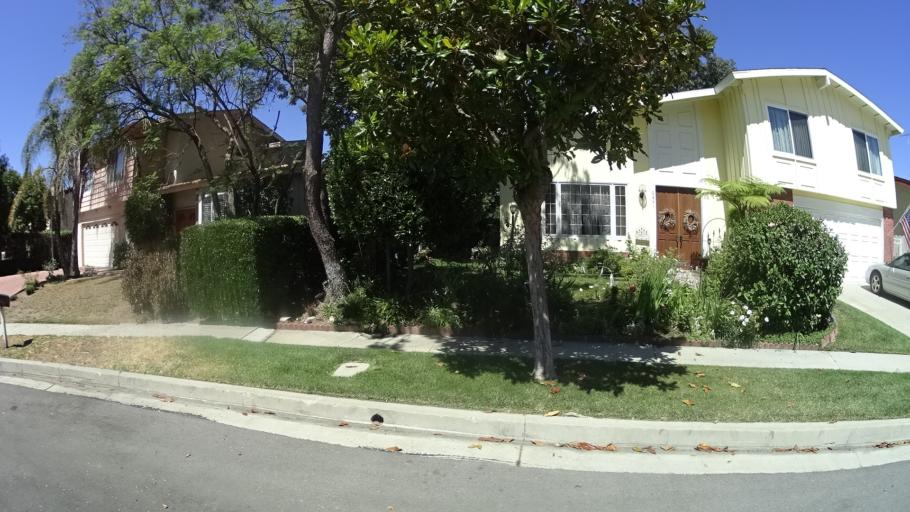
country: US
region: California
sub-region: Los Angeles County
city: Van Nuys
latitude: 34.1951
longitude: -118.4982
